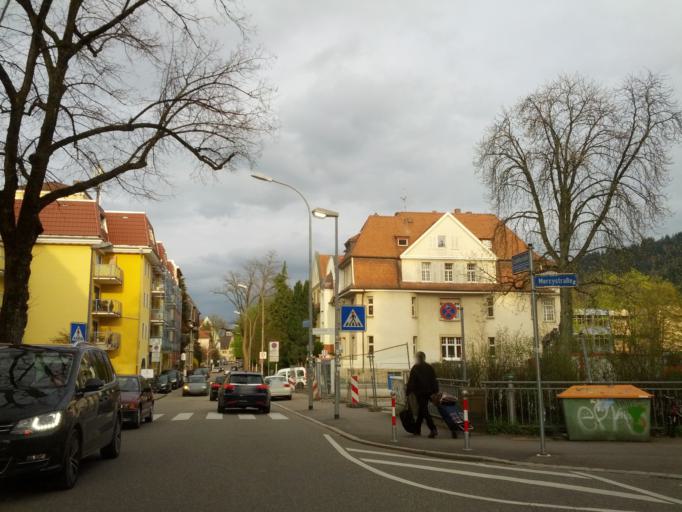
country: DE
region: Baden-Wuerttemberg
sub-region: Freiburg Region
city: Freiburg
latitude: 47.9847
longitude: 7.8407
